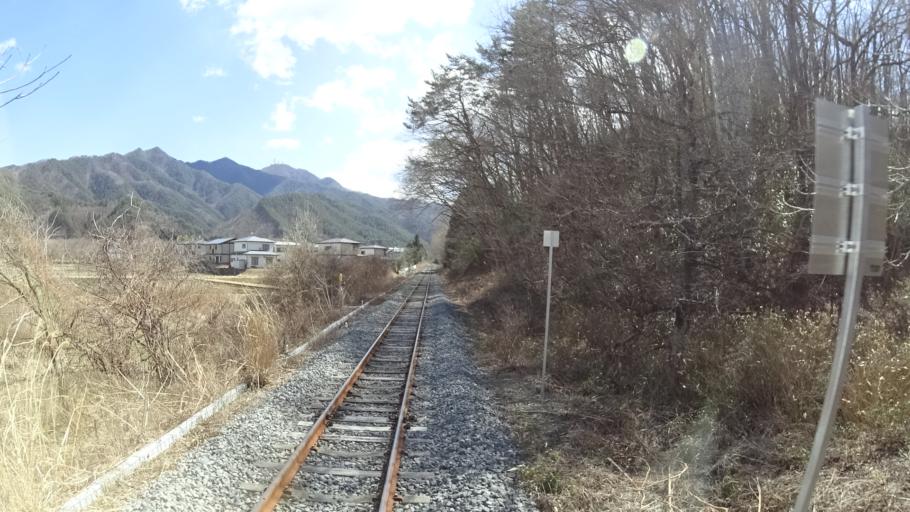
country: JP
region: Iwate
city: Miyako
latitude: 39.5614
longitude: 141.9357
